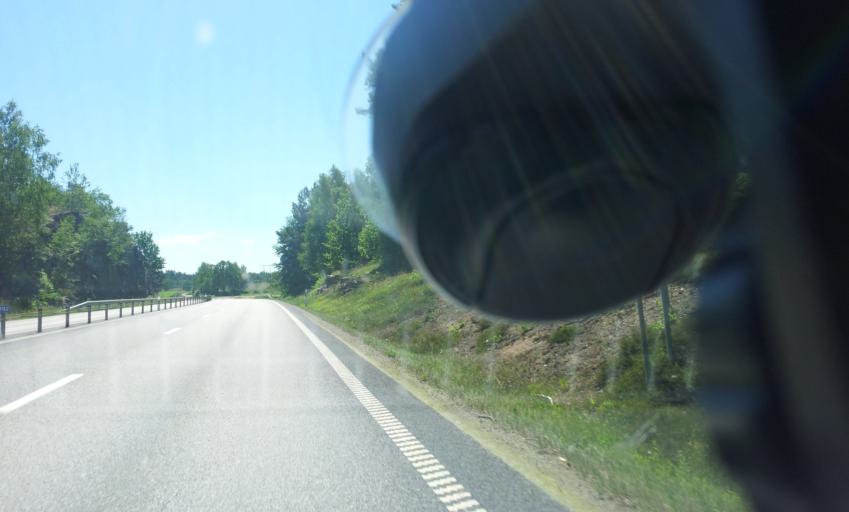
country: SE
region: Kalmar
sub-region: Vasterviks Kommun
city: Forserum
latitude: 57.9943
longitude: 16.4853
